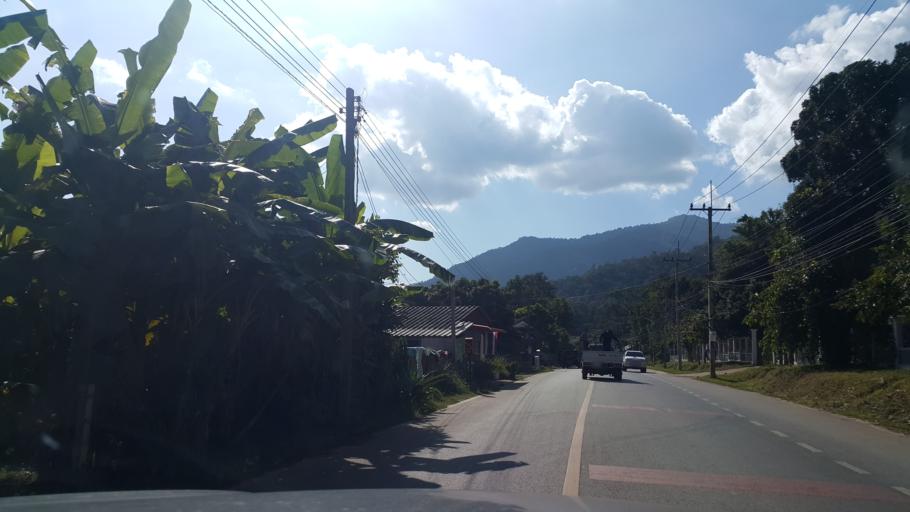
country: TH
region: Lamphun
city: Mae Tha
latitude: 18.5441
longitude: 99.2423
